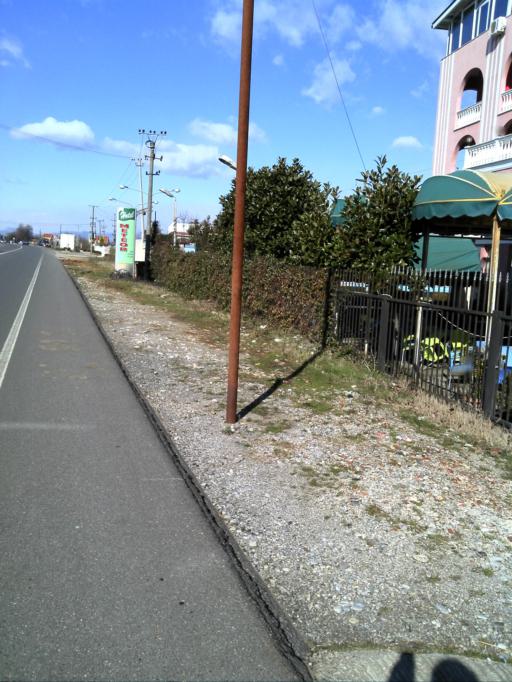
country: AL
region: Shkoder
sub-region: Rrethi i Shkodres
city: Shkoder
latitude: 42.1075
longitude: 19.5029
